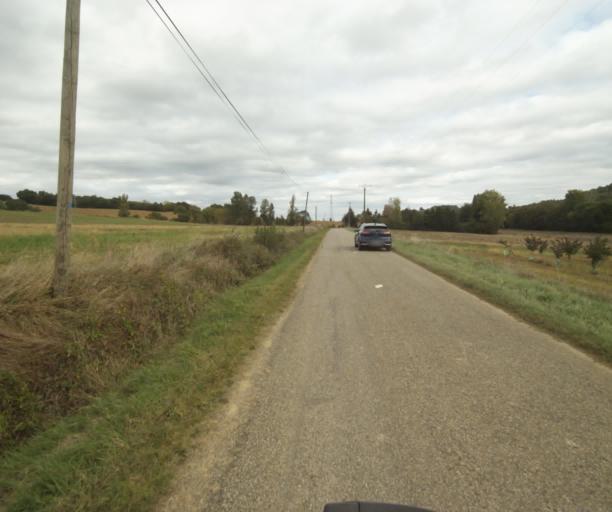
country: FR
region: Midi-Pyrenees
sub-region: Departement du Tarn-et-Garonne
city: Beaumont-de-Lomagne
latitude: 43.8554
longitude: 1.0915
